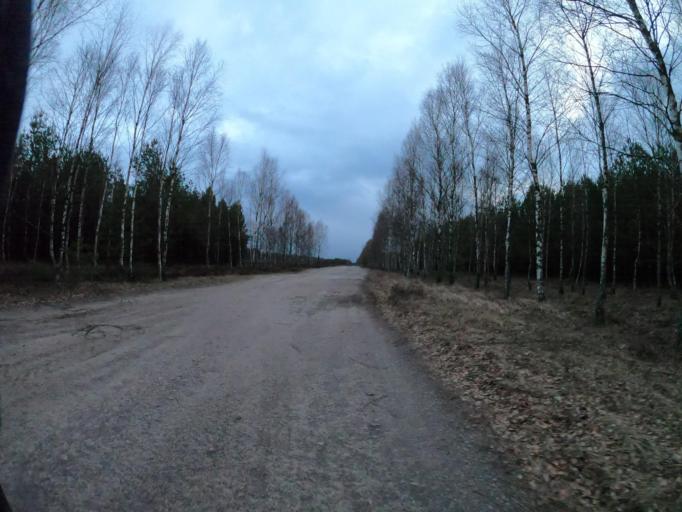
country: PL
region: West Pomeranian Voivodeship
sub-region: Powiat szczecinecki
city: Borne Sulinowo
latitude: 53.5290
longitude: 16.5728
